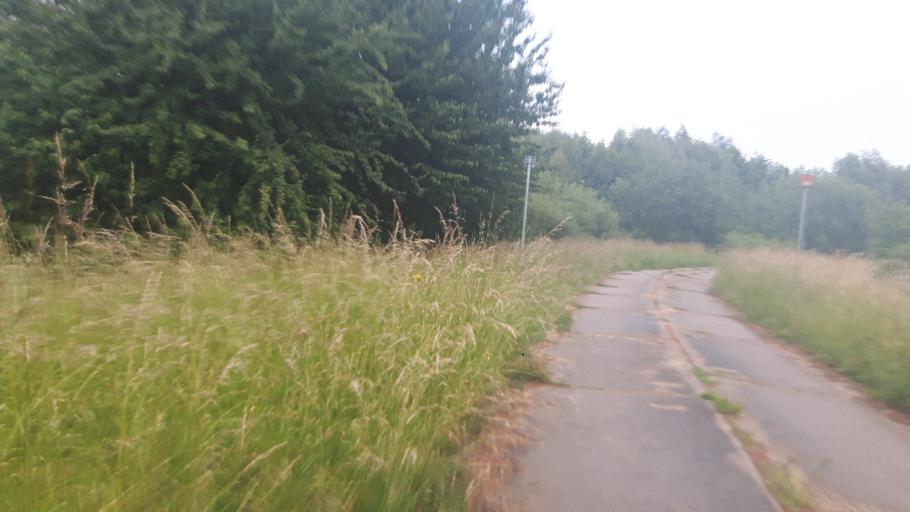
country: PL
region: Warmian-Masurian Voivodeship
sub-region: Powiat elblaski
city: Tolkmicko
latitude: 54.3222
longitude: 19.5076
